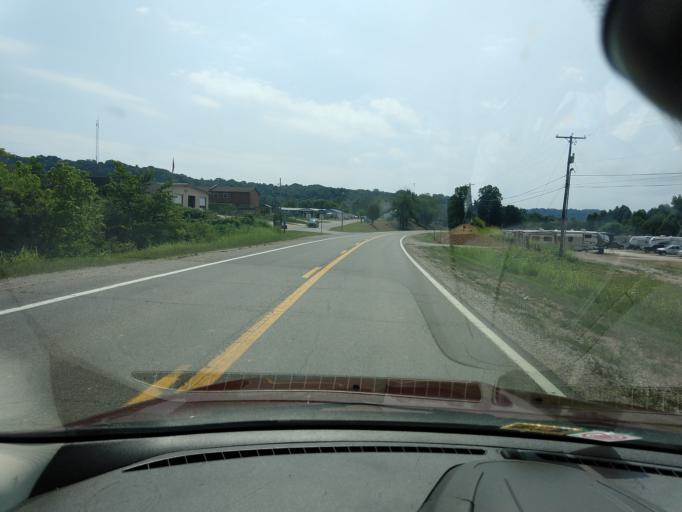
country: US
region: West Virginia
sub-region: Jackson County
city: Ravenswood
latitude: 38.8783
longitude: -81.8299
